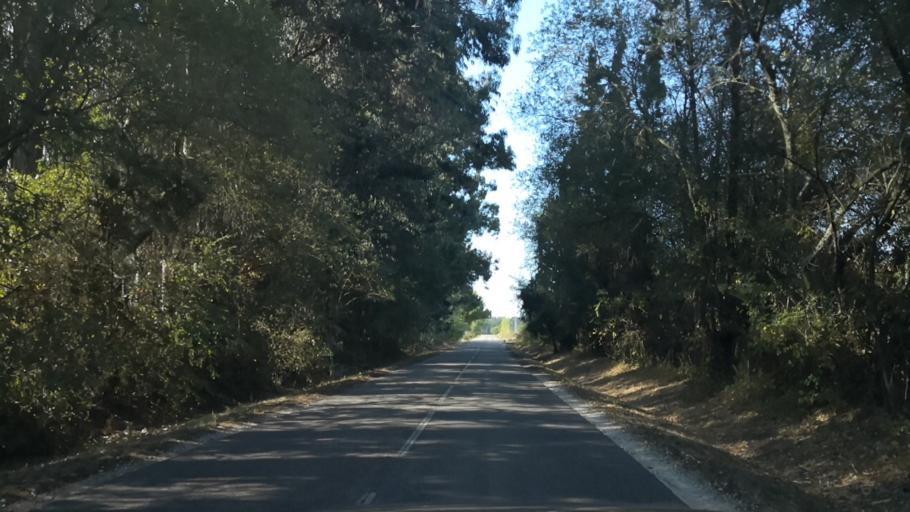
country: PT
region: Santarem
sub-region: Coruche
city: Coruche
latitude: 38.8720
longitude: -8.5382
